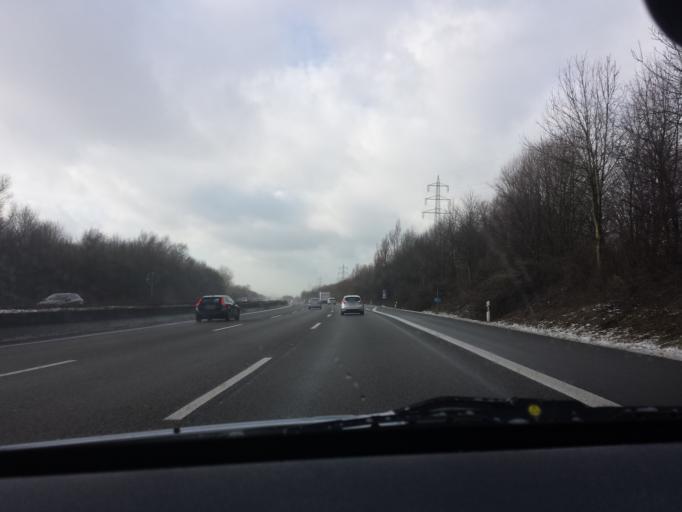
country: DE
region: North Rhine-Westphalia
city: Haan
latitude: 51.2074
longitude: 7.0232
